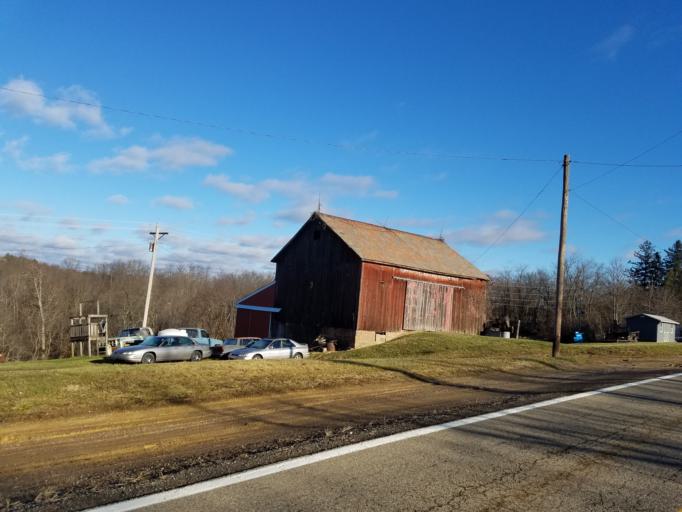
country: US
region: Ohio
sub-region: Coshocton County
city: Coshocton
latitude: 40.2534
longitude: -81.9516
